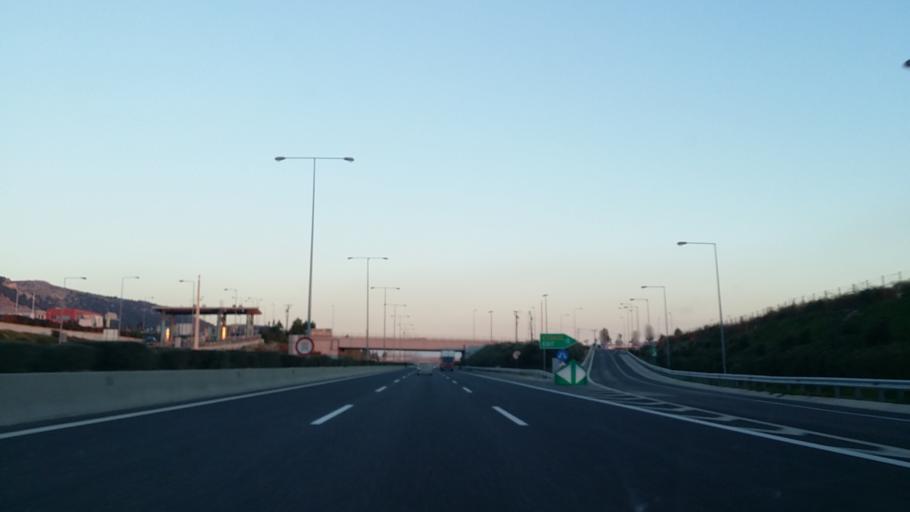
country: GR
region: Attica
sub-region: Nomarchia Dytikis Attikis
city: Aspropyrgos
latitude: 38.0905
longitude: 23.6174
